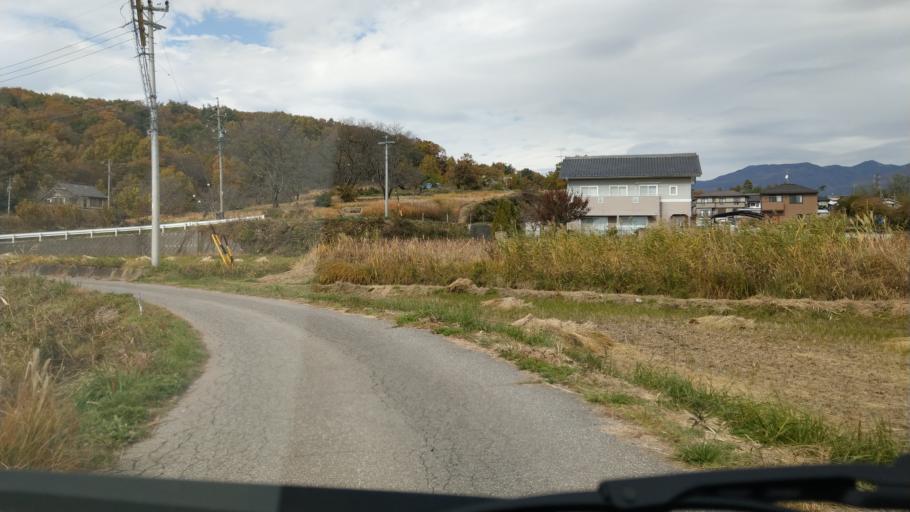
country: JP
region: Nagano
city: Komoro
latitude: 36.3057
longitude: 138.4384
